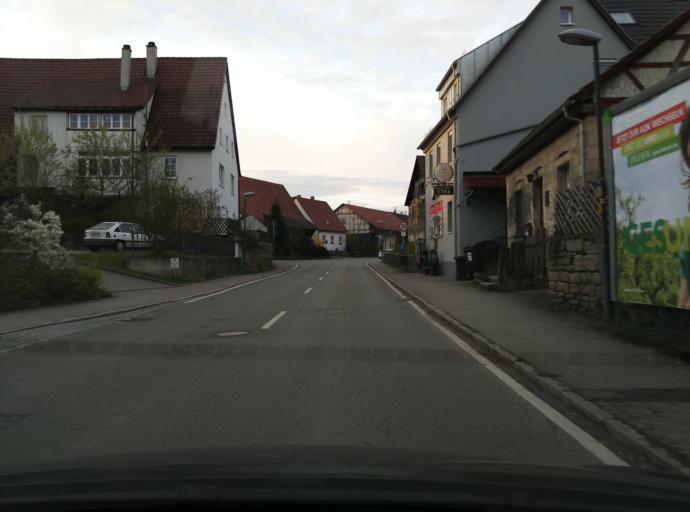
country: DE
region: Baden-Wuerttemberg
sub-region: Tuebingen Region
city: Kusterdingen
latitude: 48.5205
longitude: 9.1209
